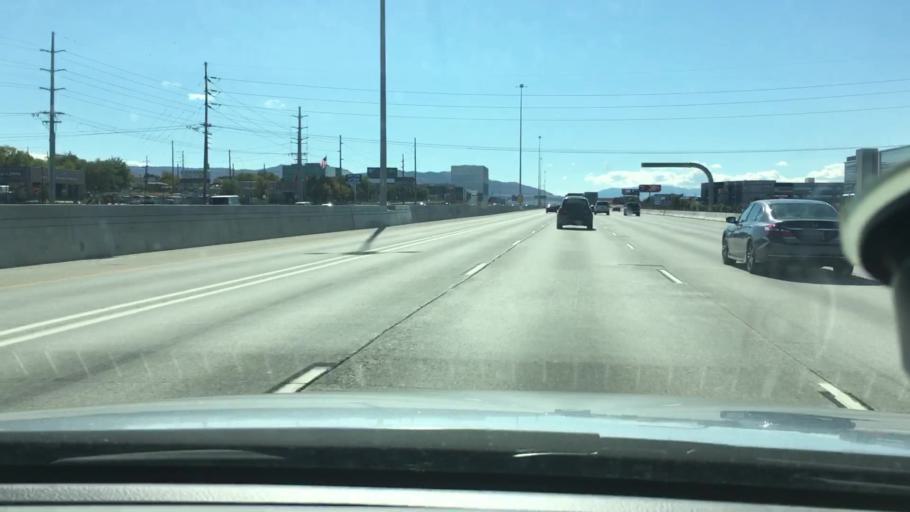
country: US
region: Utah
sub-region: Salt Lake County
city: Sandy City
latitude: 40.5817
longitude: -111.9003
